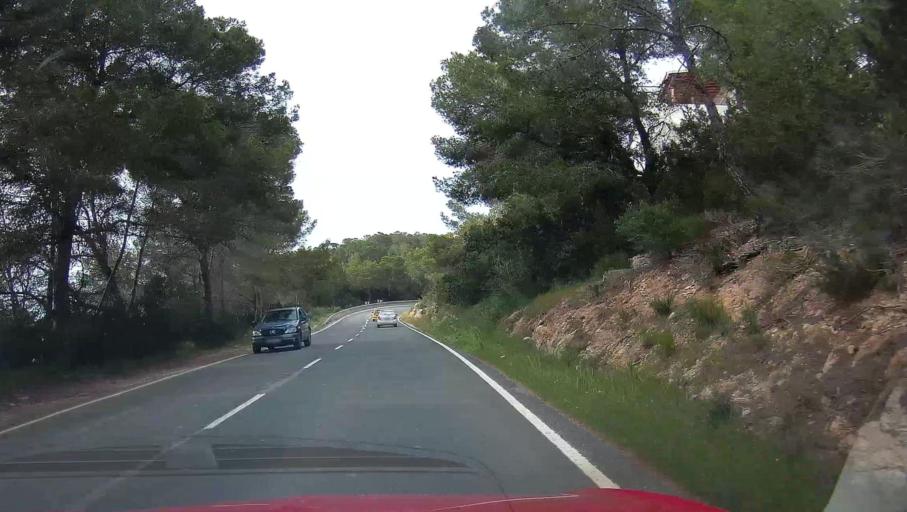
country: ES
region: Balearic Islands
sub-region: Illes Balears
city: Sant Joan de Labritja
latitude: 39.1023
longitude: 1.5107
